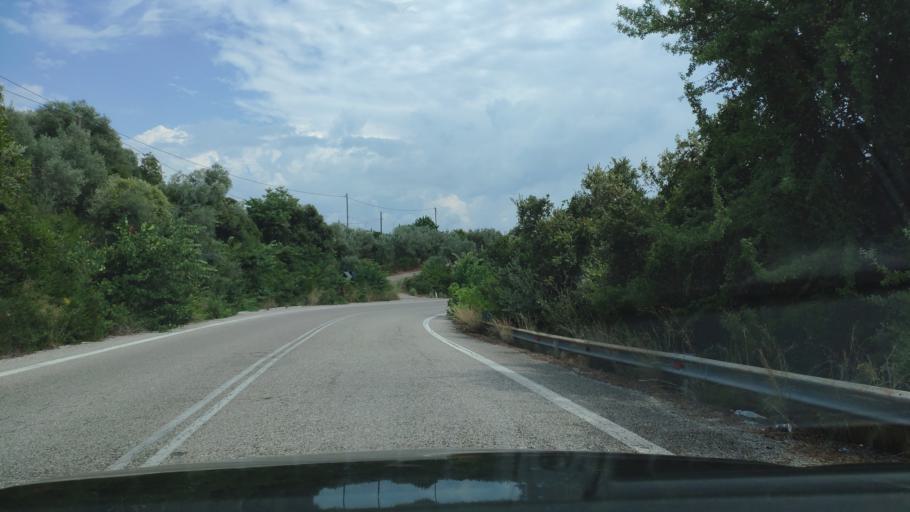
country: GR
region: West Greece
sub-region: Nomos Aitolias kai Akarnanias
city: Menidi
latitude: 39.0002
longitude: 21.1500
